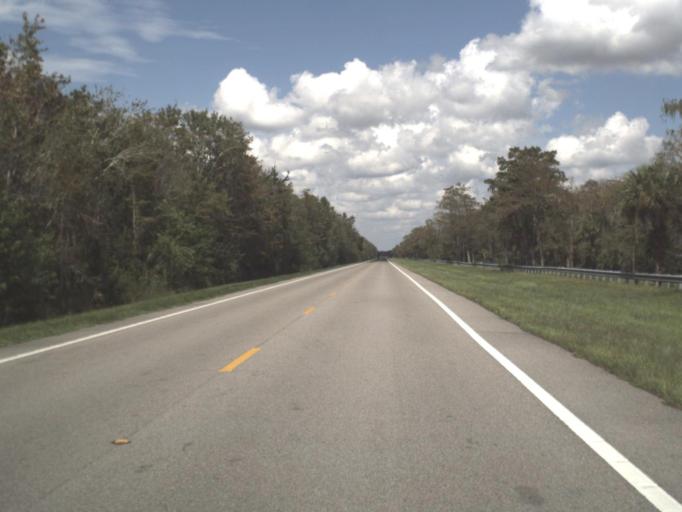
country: US
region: Florida
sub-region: Collier County
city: Immokalee
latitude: 26.2264
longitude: -81.3441
